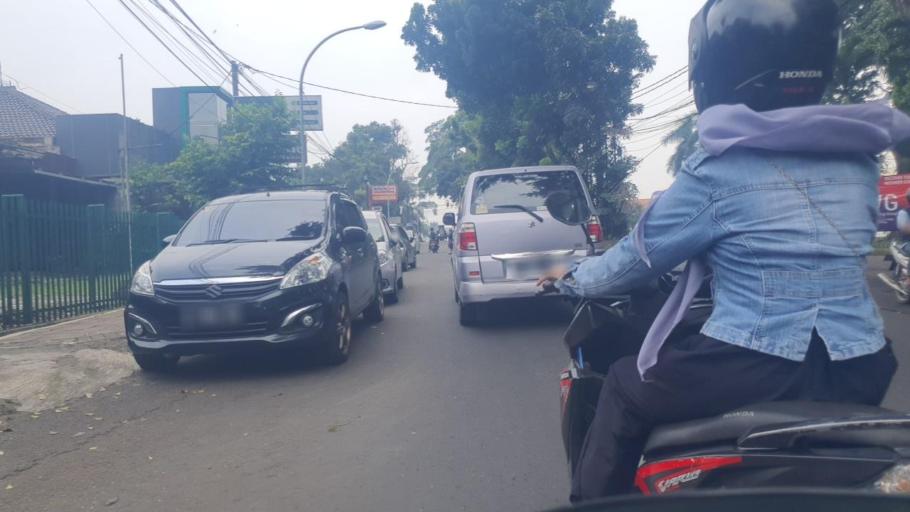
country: ID
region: West Java
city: Bogor
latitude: -6.5839
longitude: 106.7878
